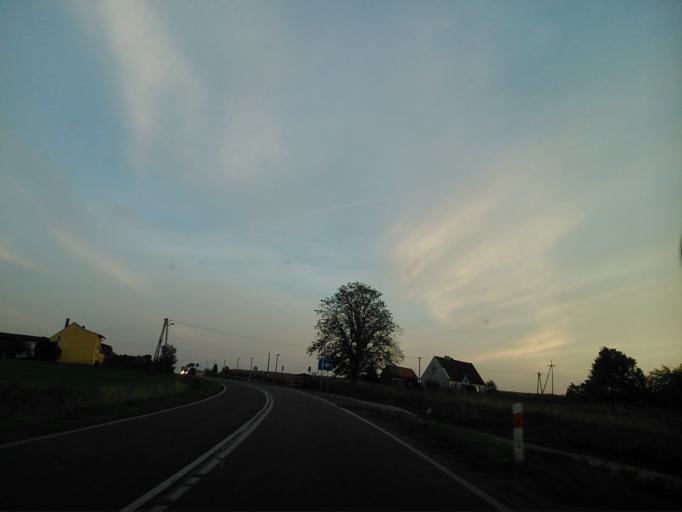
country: PL
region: Kujawsko-Pomorskie
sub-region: Powiat wabrzeski
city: Debowa Laka
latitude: 53.1996
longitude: 19.0369
